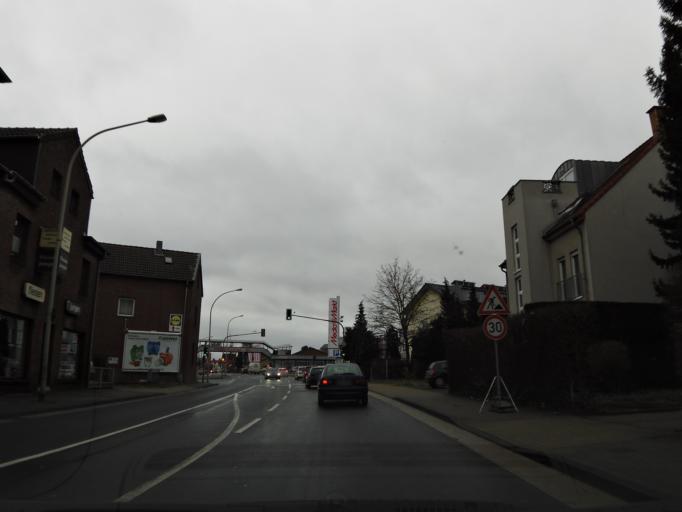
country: NL
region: Limburg
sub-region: Gemeente Kerkrade
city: Kerkrade
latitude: 50.8529
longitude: 6.0768
